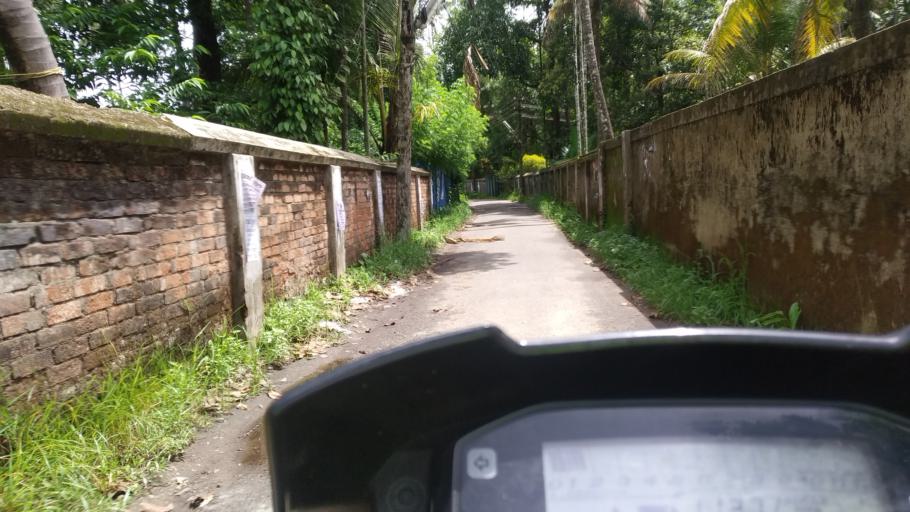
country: IN
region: Kerala
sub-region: Ernakulam
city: Elur
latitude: 10.0841
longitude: 76.2113
